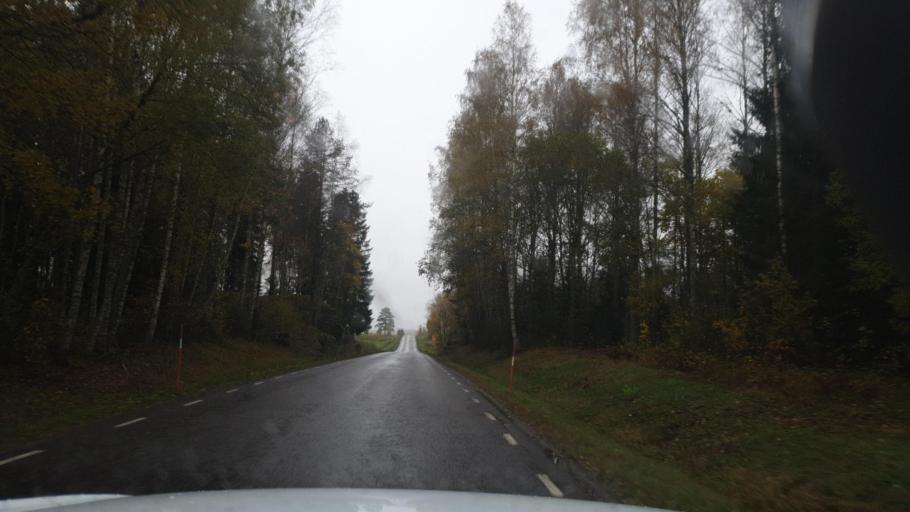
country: SE
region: Vaermland
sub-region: Eda Kommun
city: Charlottenberg
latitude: 59.7902
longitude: 12.1555
